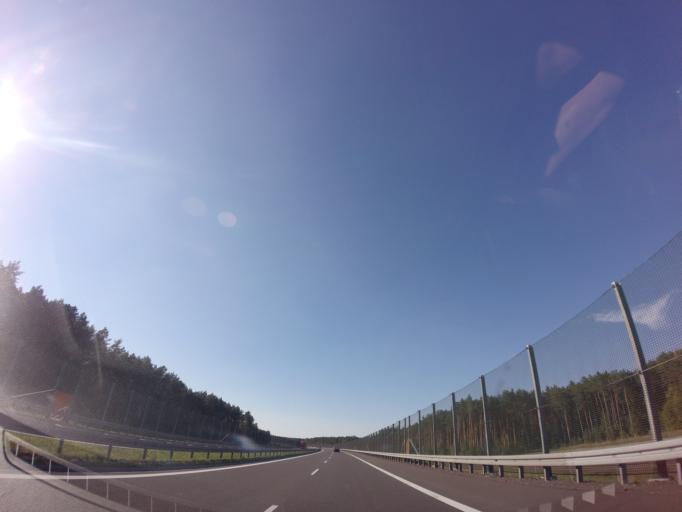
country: PL
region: Lubusz
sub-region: Powiat miedzyrzecki
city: Skwierzyna
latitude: 52.5715
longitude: 15.4710
